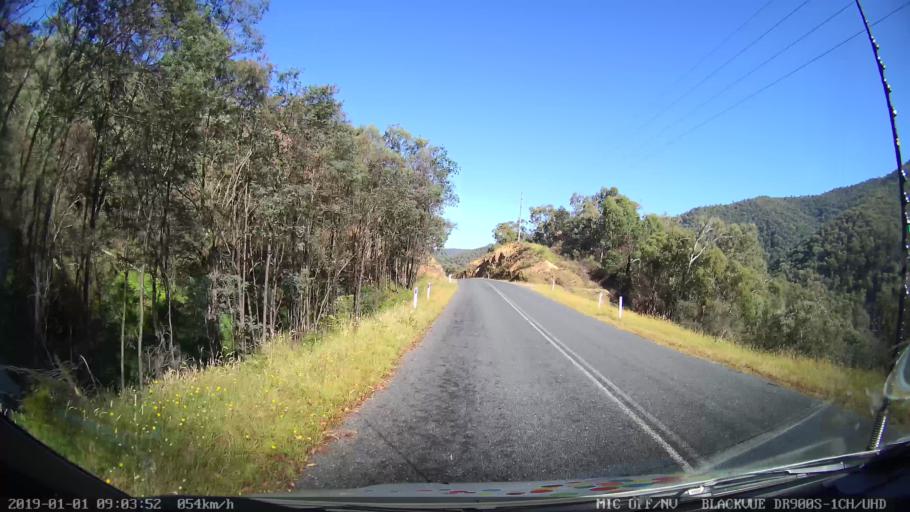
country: AU
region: New South Wales
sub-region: Snowy River
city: Jindabyne
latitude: -36.2222
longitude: 148.1612
